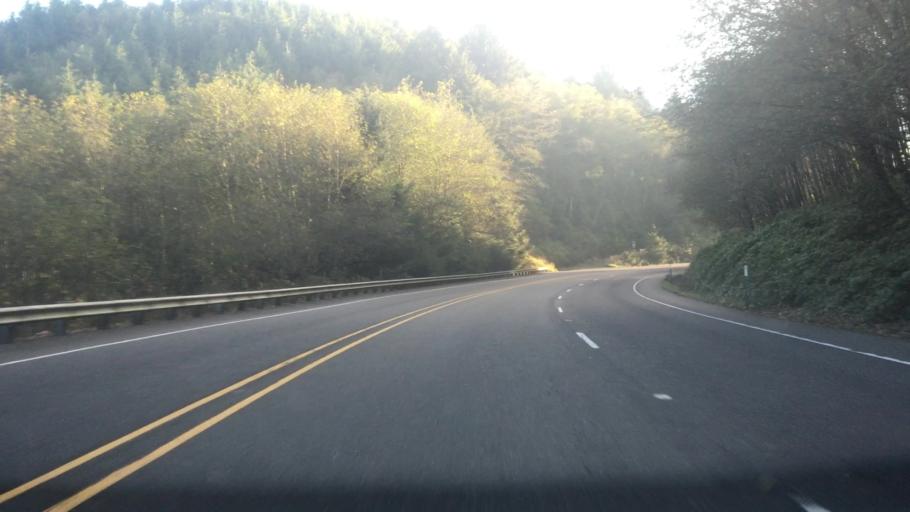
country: US
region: Oregon
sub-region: Clatsop County
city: Cannon Beach
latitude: 45.9159
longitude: -123.9388
